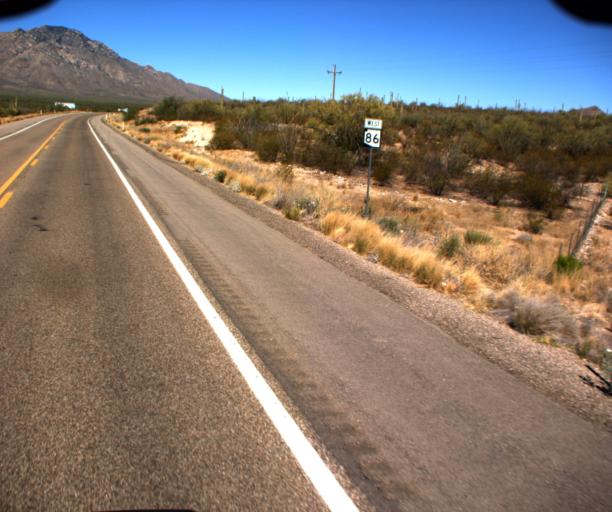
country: US
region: Arizona
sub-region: Pima County
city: Three Points
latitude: 32.0432
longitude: -111.4389
